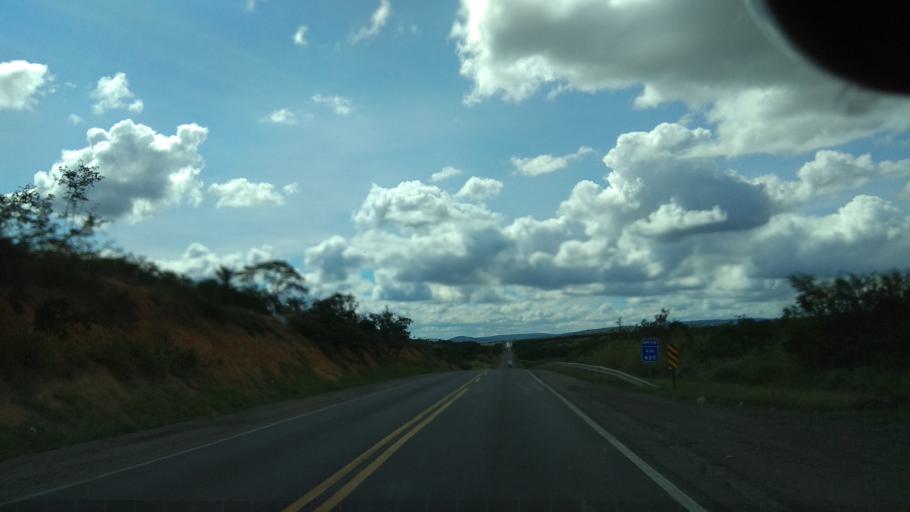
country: BR
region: Bahia
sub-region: Jaguaquara
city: Jaguaquara
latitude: -13.4534
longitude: -40.0320
